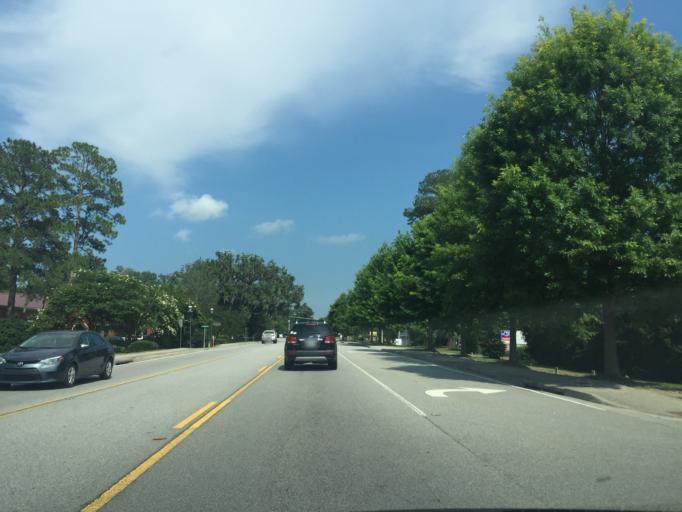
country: US
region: Georgia
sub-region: Chatham County
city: Isle of Hope
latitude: 32.0114
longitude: -81.1046
